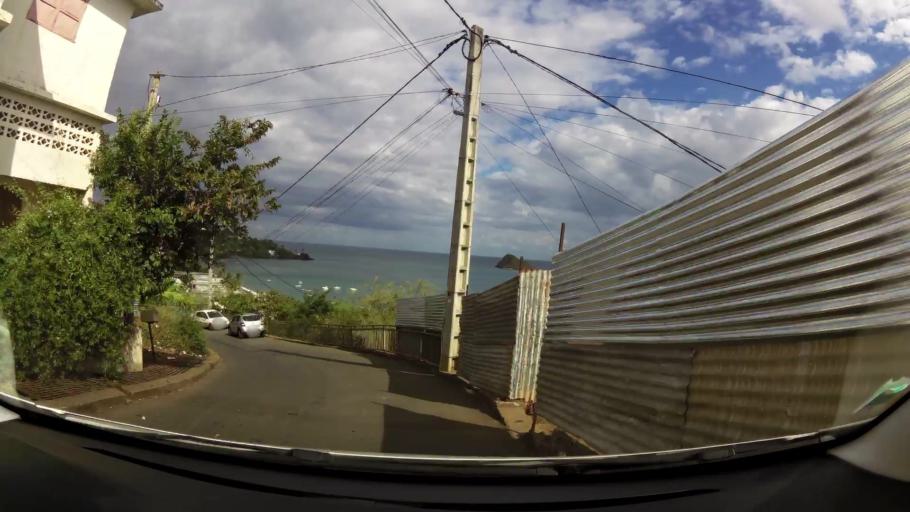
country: YT
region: Sada
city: Sada
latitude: -12.8474
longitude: 45.1015
